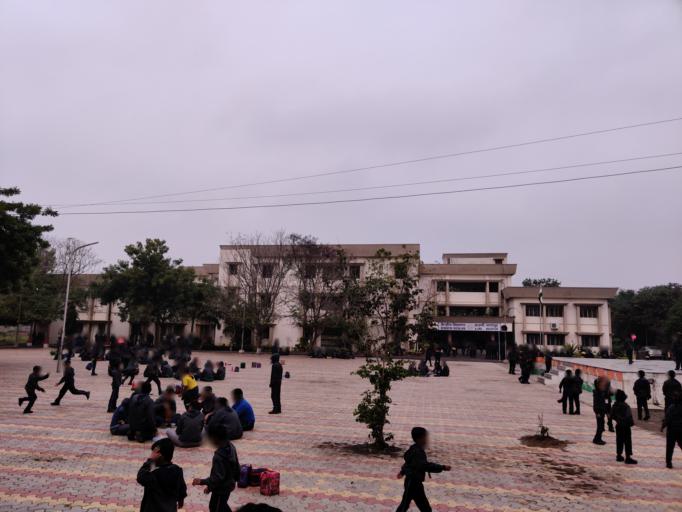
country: IN
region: Maharashtra
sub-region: Nagpur Division
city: Nagpur
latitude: 21.1244
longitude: 79.0903
